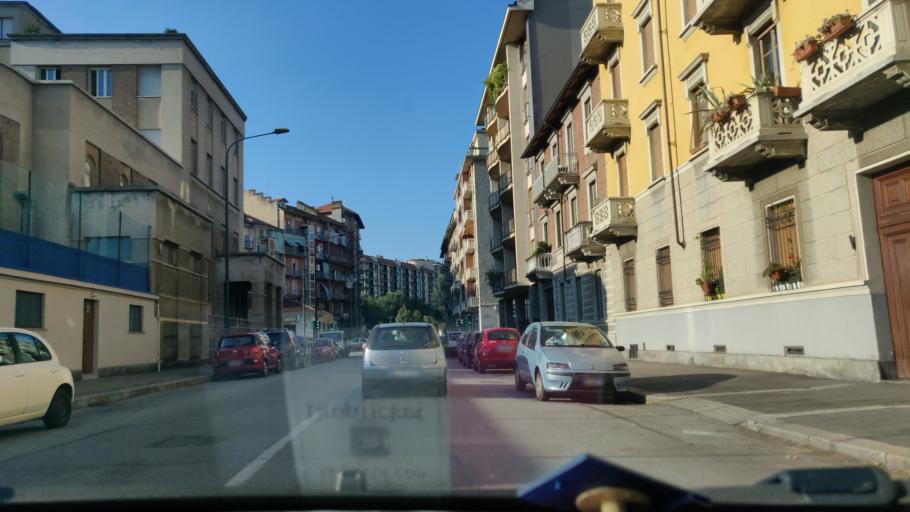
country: IT
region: Piedmont
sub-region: Provincia di Torino
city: Lesna
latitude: 45.0720
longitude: 7.6423
